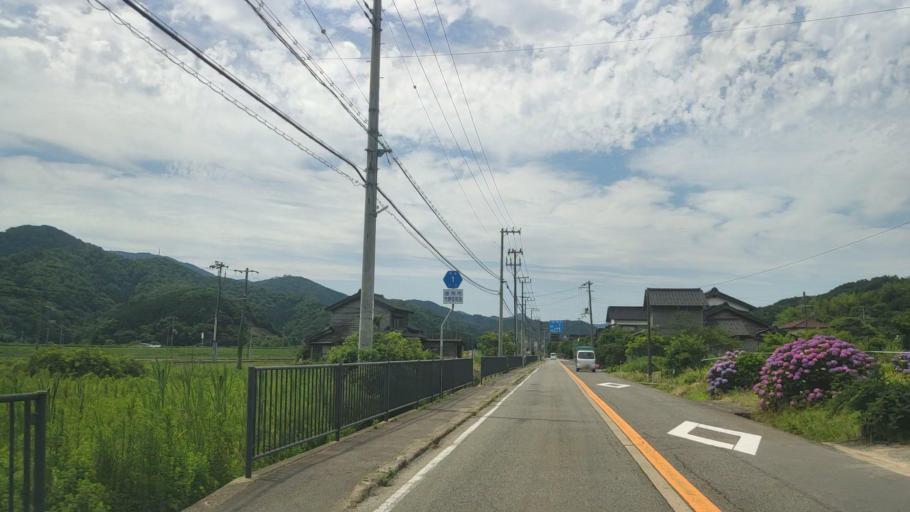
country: JP
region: Hyogo
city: Toyooka
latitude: 35.6448
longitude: 134.7581
